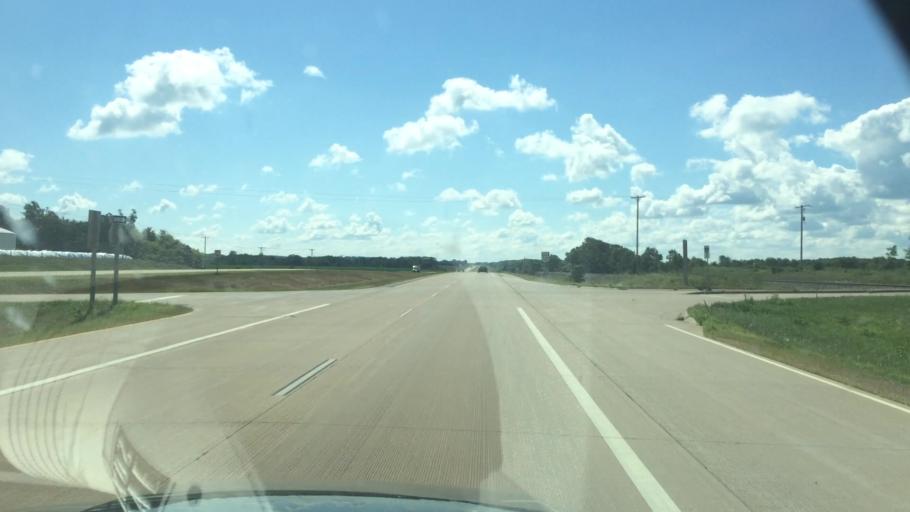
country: US
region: Wisconsin
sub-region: Portage County
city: Amherst
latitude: 44.4943
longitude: -89.3666
